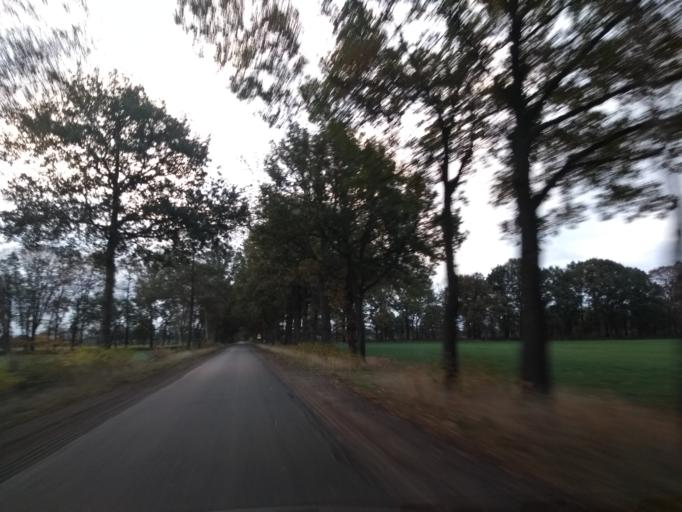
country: NL
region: Gelderland
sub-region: Gemeente Bronckhorst
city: Zelhem
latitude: 52.0213
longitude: 6.3684
